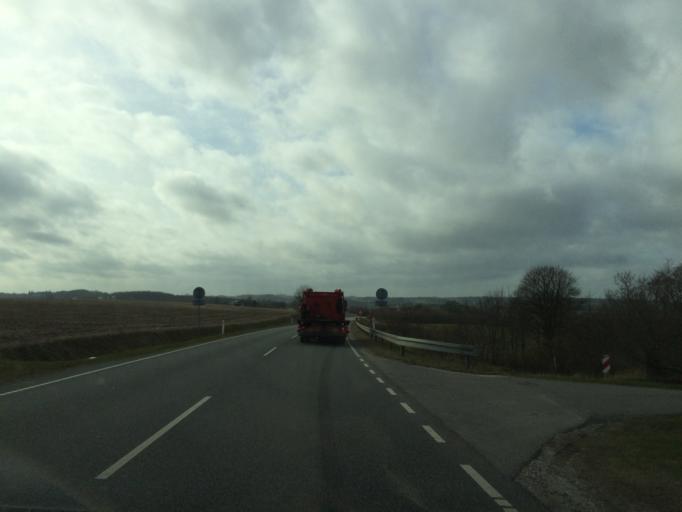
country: DK
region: Central Jutland
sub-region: Randers Kommune
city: Langa
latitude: 56.4805
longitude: 9.8812
